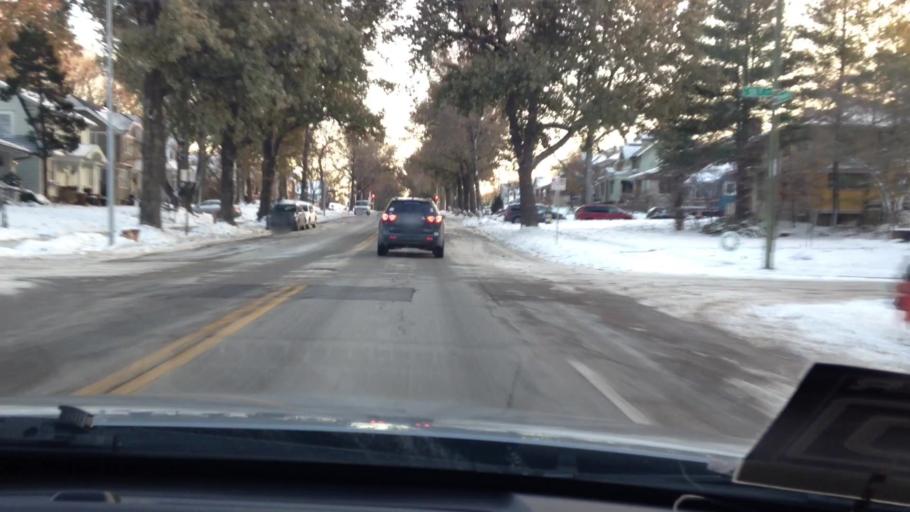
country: US
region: Kansas
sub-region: Johnson County
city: Mission Hills
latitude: 39.0221
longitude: -94.5764
